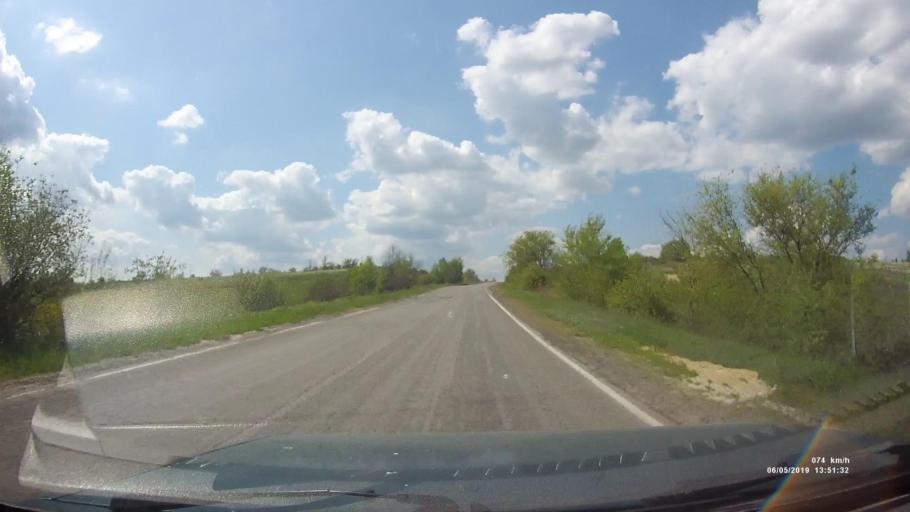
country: RU
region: Rostov
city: Melikhovskaya
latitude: 47.6574
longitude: 40.4906
